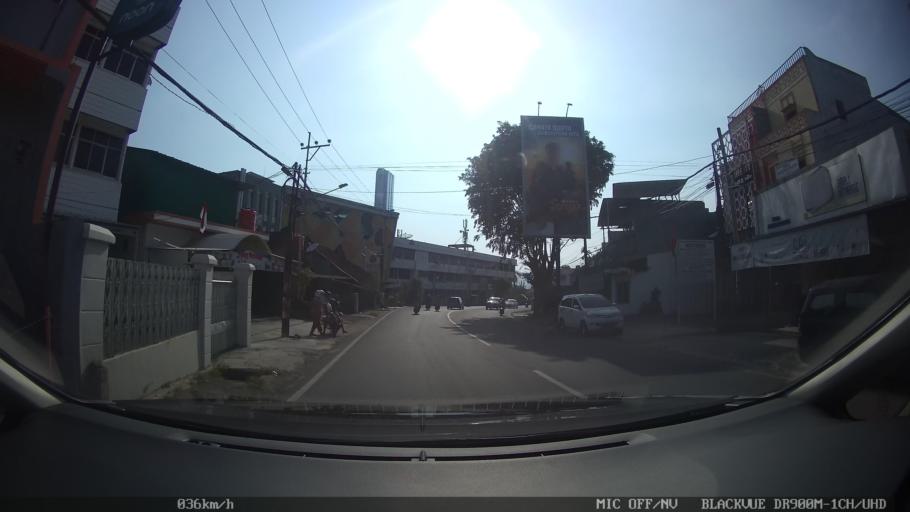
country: ID
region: Lampung
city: Bandarlampung
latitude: -5.4191
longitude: 105.2497
